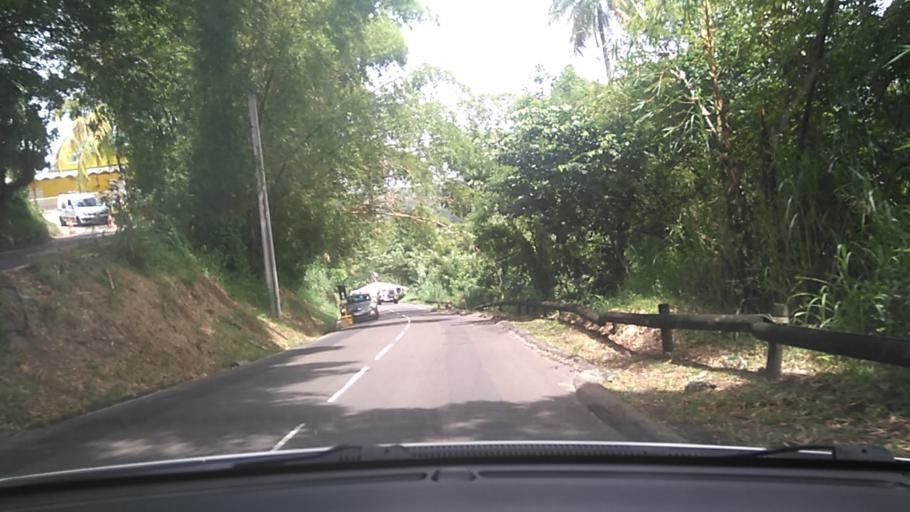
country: MQ
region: Martinique
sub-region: Martinique
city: Saint-Esprit
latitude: 14.5608
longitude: -60.9328
